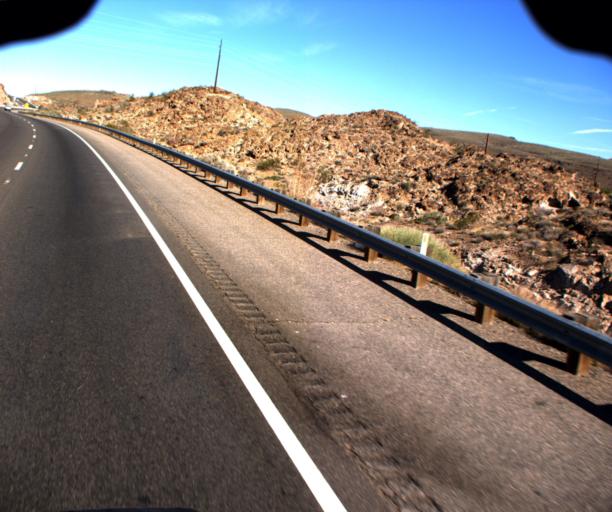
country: US
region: Arizona
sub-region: Mohave County
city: Kingman
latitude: 35.2017
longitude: -114.0823
